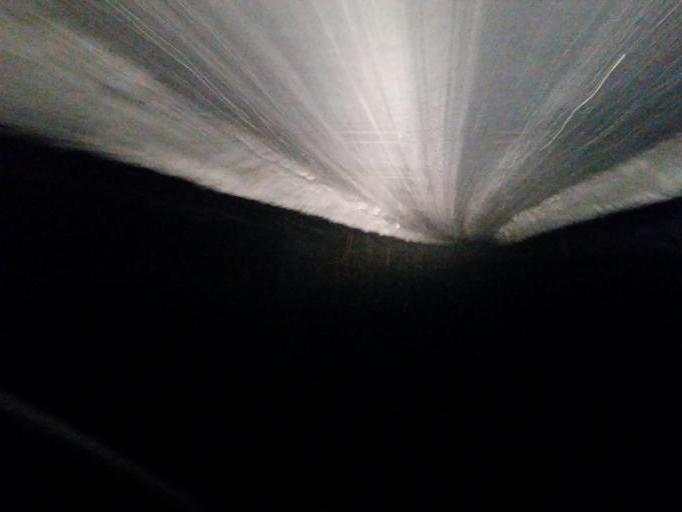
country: SE
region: Norrbotten
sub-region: Alvsbyns Kommun
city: AElvsbyn
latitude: 65.6130
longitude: 20.8914
